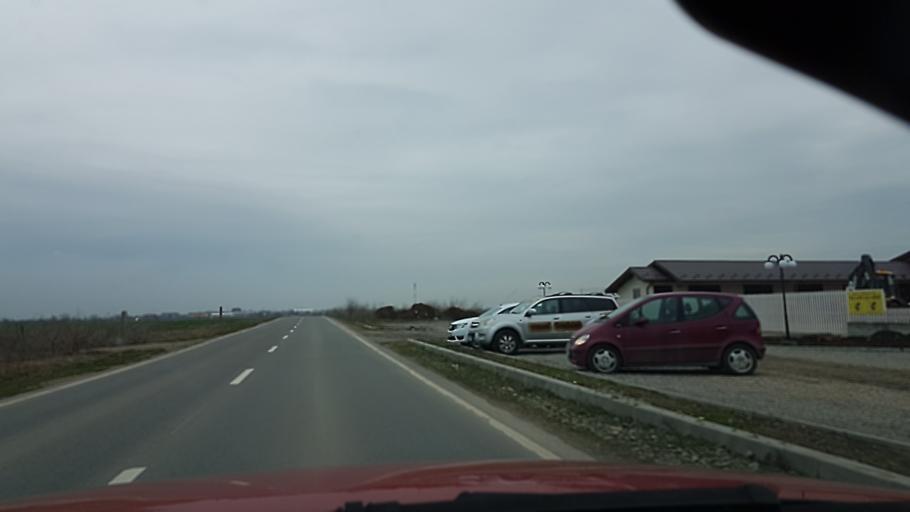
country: RO
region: Ilfov
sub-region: Comuna Balotesti
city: Balotesti
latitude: 44.6052
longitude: 26.1306
